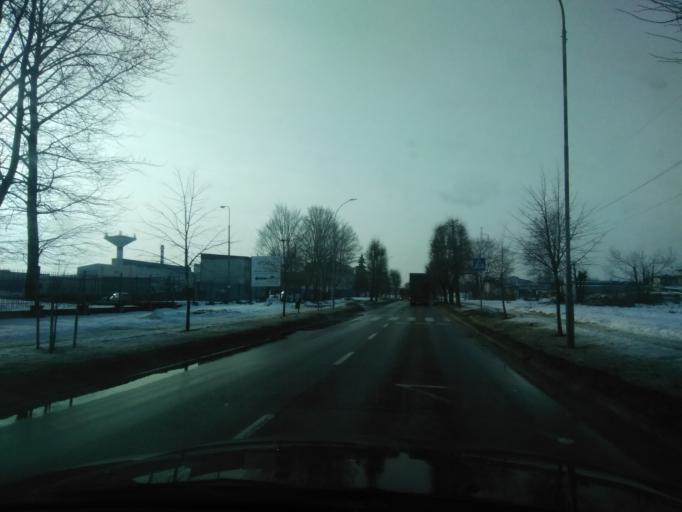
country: PL
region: Subcarpathian Voivodeship
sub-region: Krosno
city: Krosno
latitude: 49.7021
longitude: 21.7367
